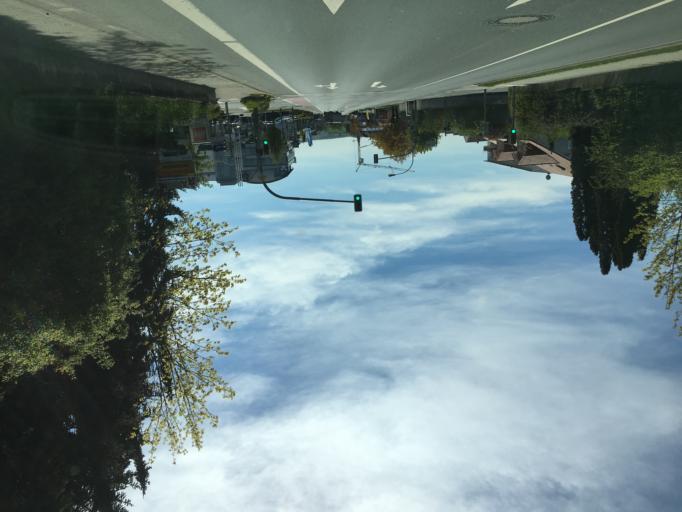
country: DE
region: Hesse
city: Reinheim
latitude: 49.8339
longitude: 8.8335
